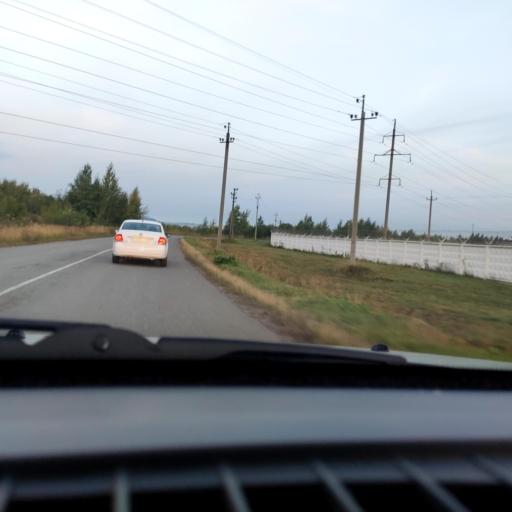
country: RU
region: Perm
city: Gamovo
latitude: 57.9027
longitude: 56.1300
